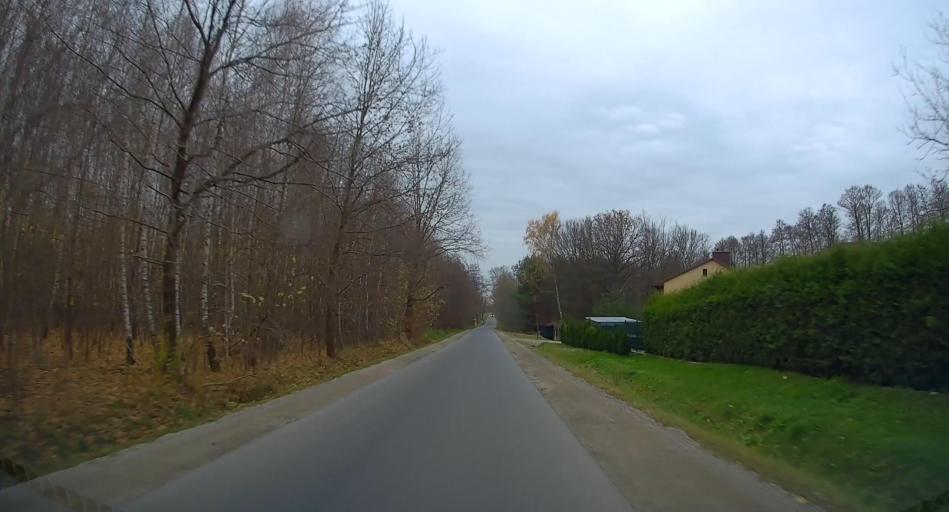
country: PL
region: Lodz Voivodeship
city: Zabia Wola
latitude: 52.0004
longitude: 20.6581
